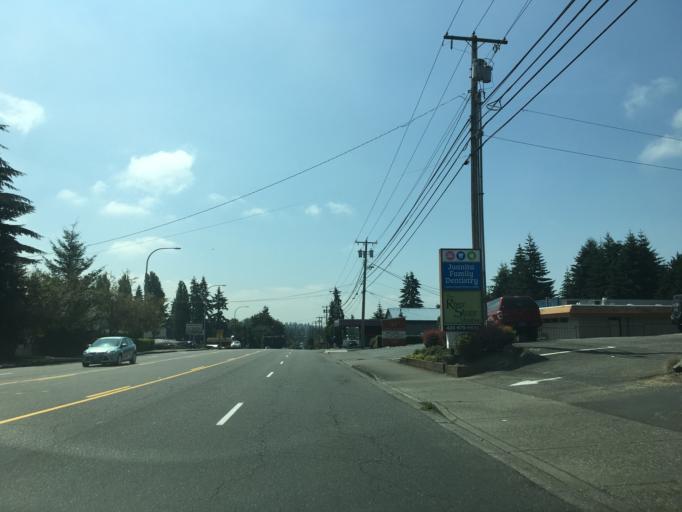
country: US
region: Washington
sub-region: King County
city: Inglewood-Finn Hill
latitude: 47.7228
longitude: -122.2078
